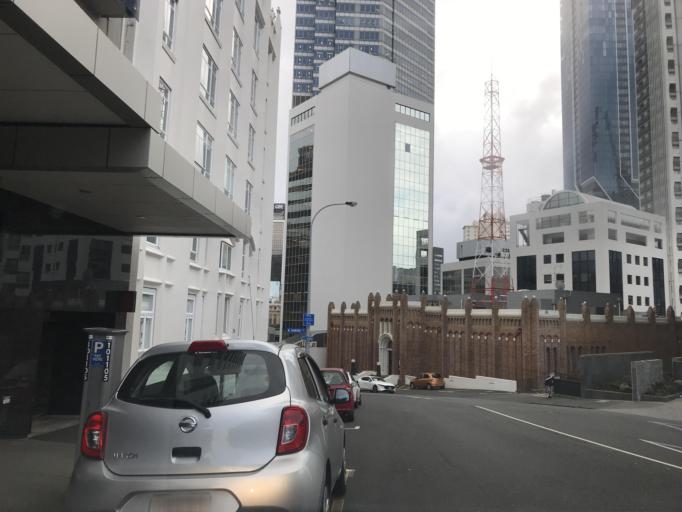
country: NZ
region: Auckland
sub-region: Auckland
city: Auckland
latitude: -36.8469
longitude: 174.7702
